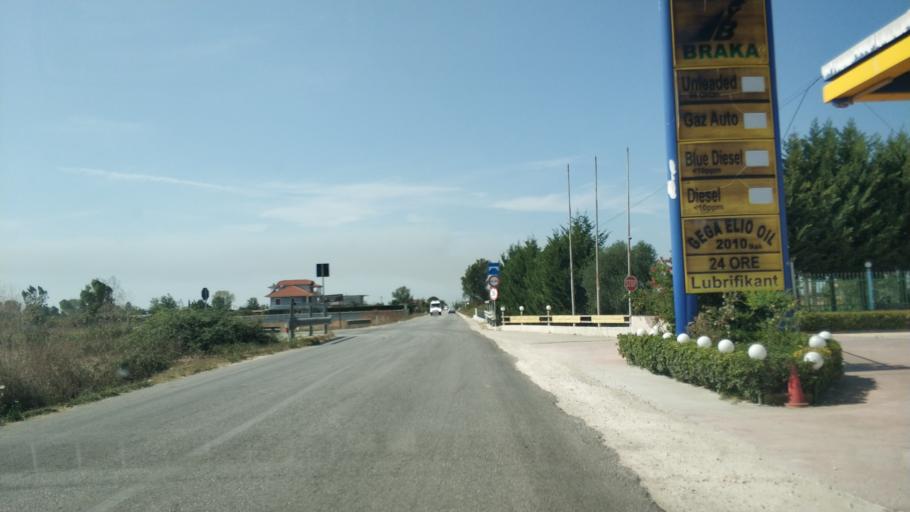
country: AL
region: Fier
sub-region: Rrethi i Fierit
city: Dermenas
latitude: 40.7473
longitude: 19.4869
